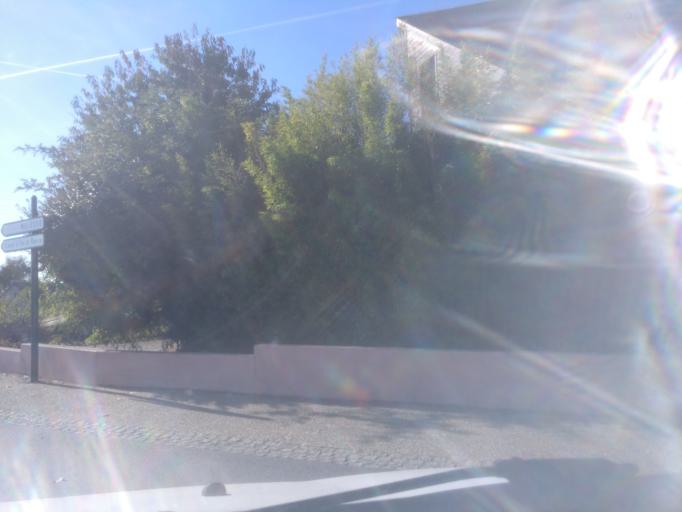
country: FR
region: Brittany
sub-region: Departement d'Ille-et-Vilaine
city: Chevaigne
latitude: 48.2090
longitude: -1.6301
